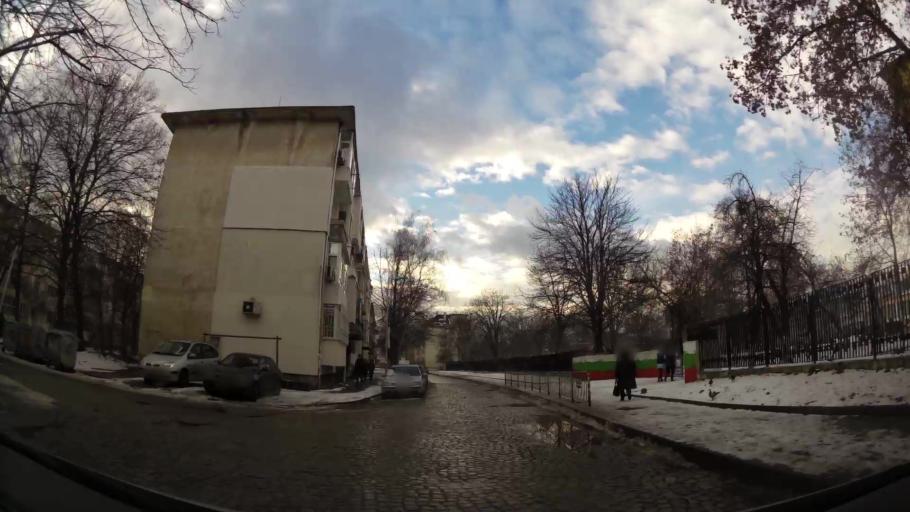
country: BG
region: Sofia-Capital
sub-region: Stolichna Obshtina
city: Sofia
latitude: 42.7056
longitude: 23.2784
